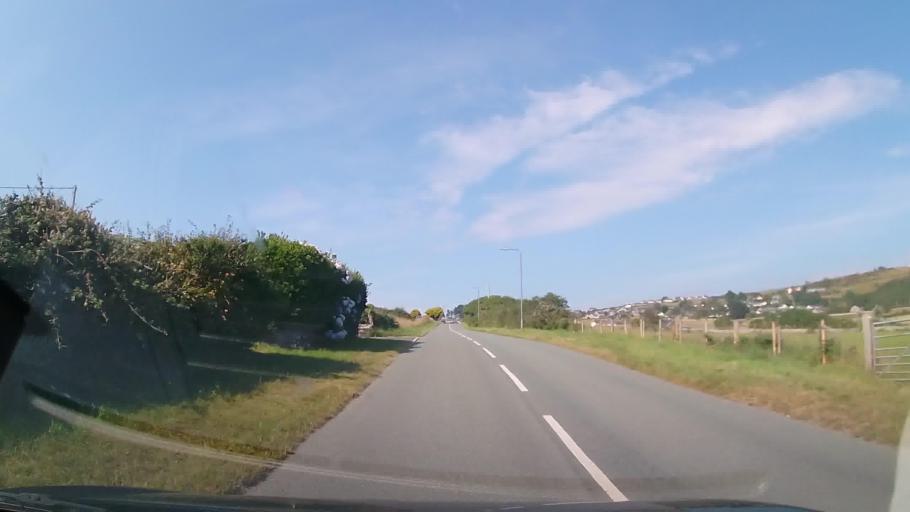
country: GB
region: Wales
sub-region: Gwynedd
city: Llanfair
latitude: 52.8388
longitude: -4.1212
